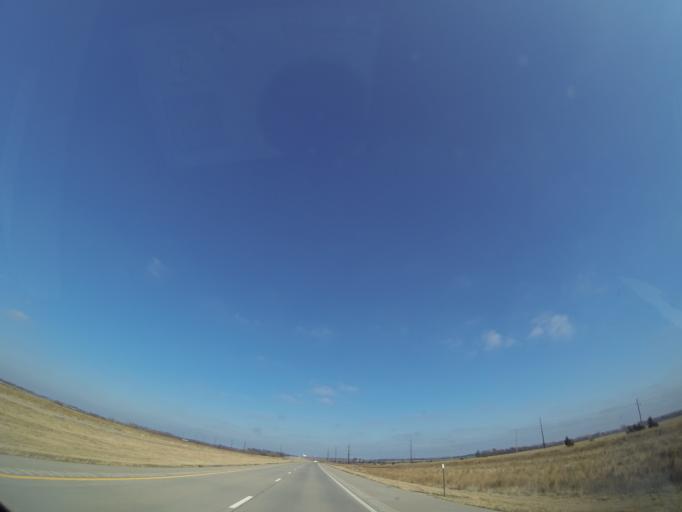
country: US
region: Kansas
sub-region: McPherson County
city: Inman
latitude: 38.1935
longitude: -97.8077
